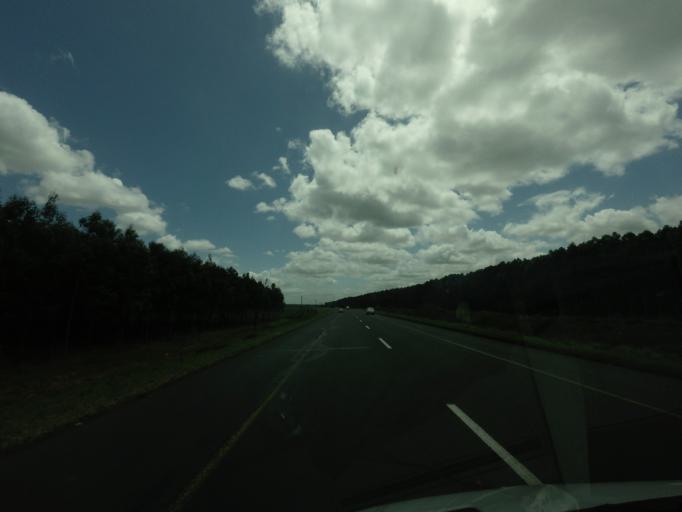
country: ZA
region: KwaZulu-Natal
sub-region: uThungulu District Municipality
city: KwaMbonambi
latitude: -28.5635
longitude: 32.1147
